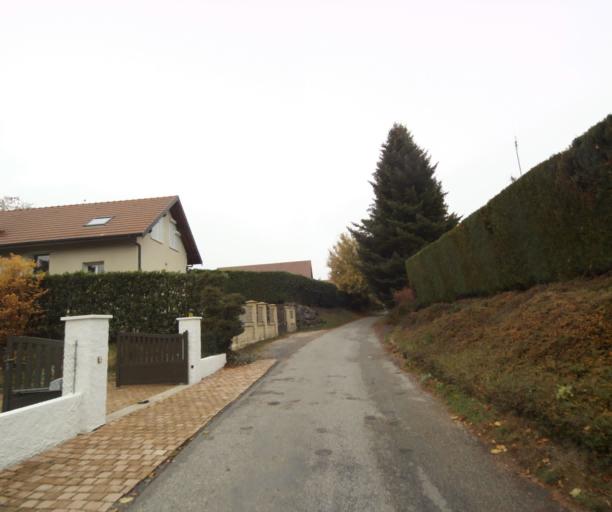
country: FR
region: Rhone-Alpes
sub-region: Departement de la Haute-Savoie
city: Reignier-Esery
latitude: 46.1393
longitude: 6.2829
